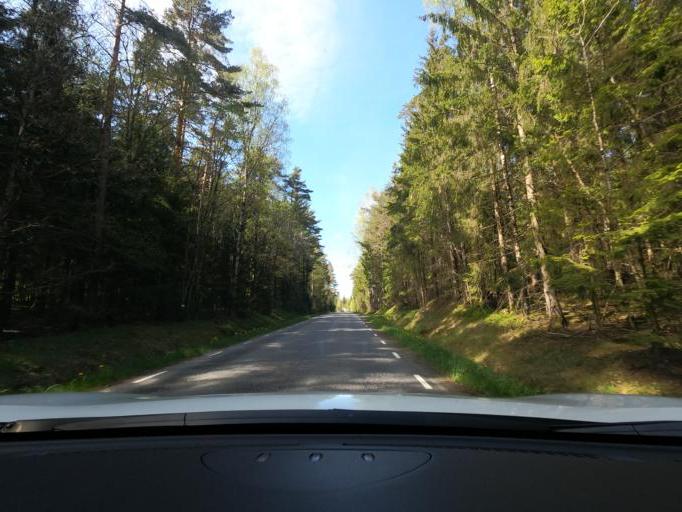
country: SE
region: Vaestra Goetaland
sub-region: Marks Kommun
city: Kinna
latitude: 57.4827
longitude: 12.5668
